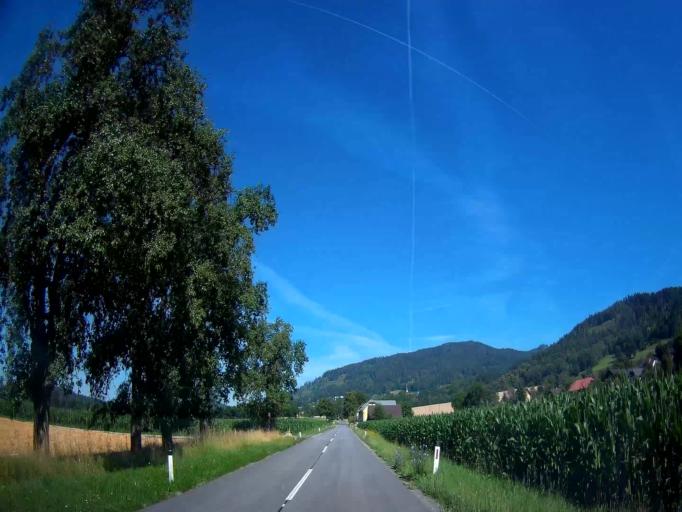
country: AT
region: Carinthia
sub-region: Politischer Bezirk Klagenfurt Land
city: Poggersdorf
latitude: 46.6992
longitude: 14.4304
